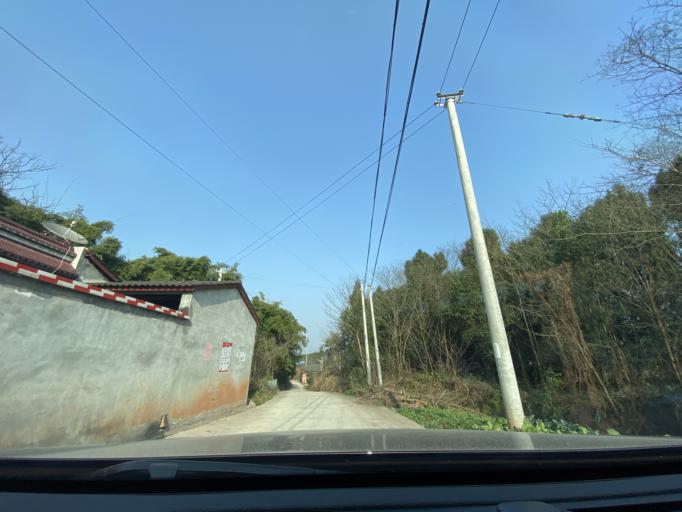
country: CN
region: Sichuan
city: Wenlin
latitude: 30.2485
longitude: 104.2487
